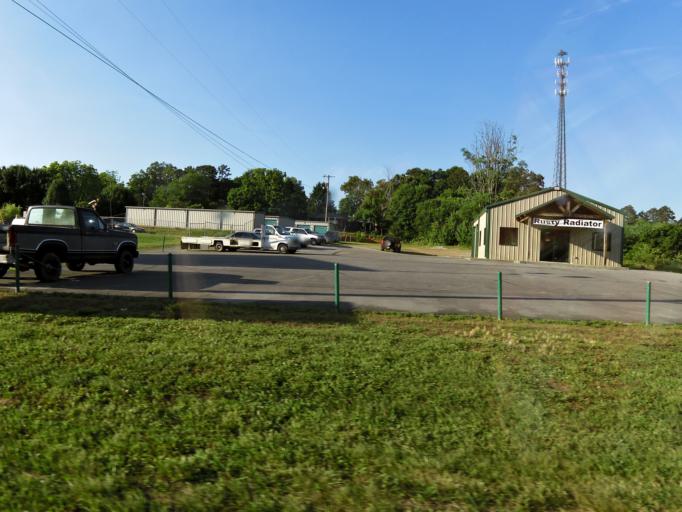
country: US
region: Tennessee
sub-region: Sevier County
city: Seymour
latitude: 35.8767
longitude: -83.7668
